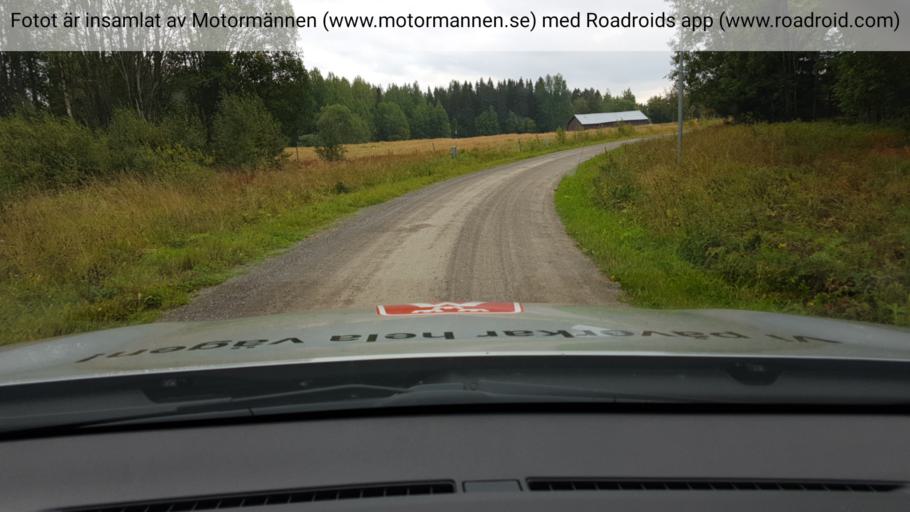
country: SE
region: Jaemtland
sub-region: Stroemsunds Kommun
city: Stroemsund
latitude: 63.7762
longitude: 15.3193
